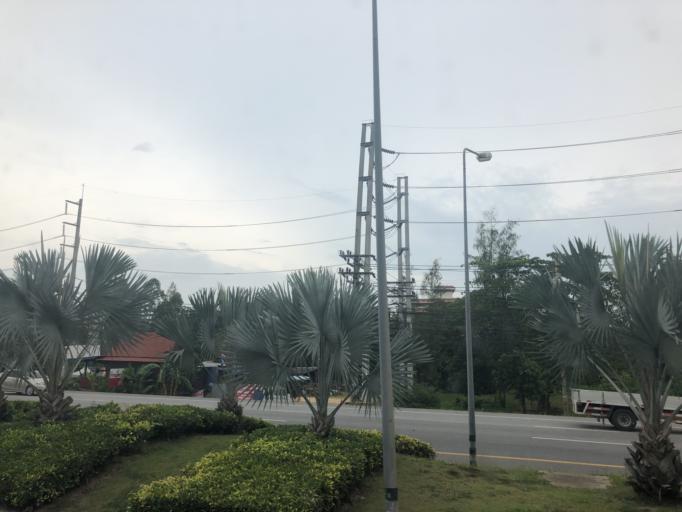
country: TH
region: Chon Buri
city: Bang Lamung
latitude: 13.0116
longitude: 100.9311
